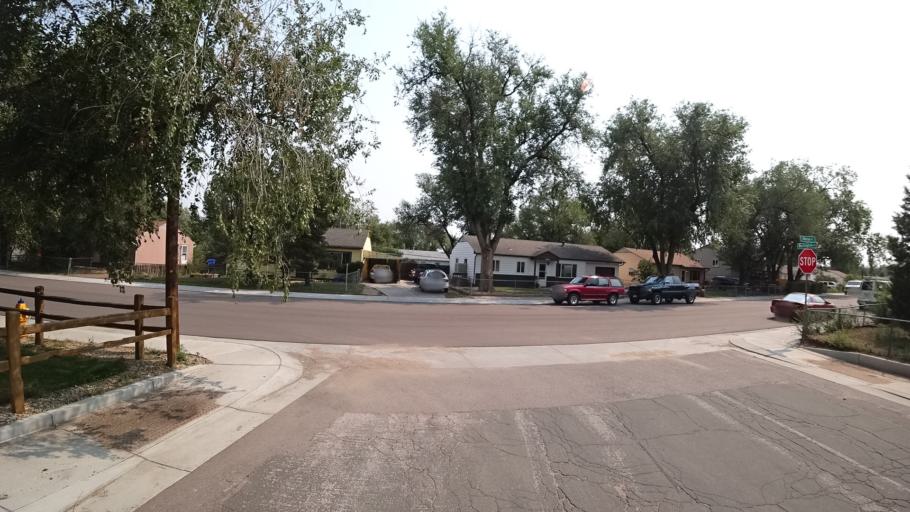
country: US
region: Colorado
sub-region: El Paso County
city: Colorado Springs
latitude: 38.8061
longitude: -104.8186
